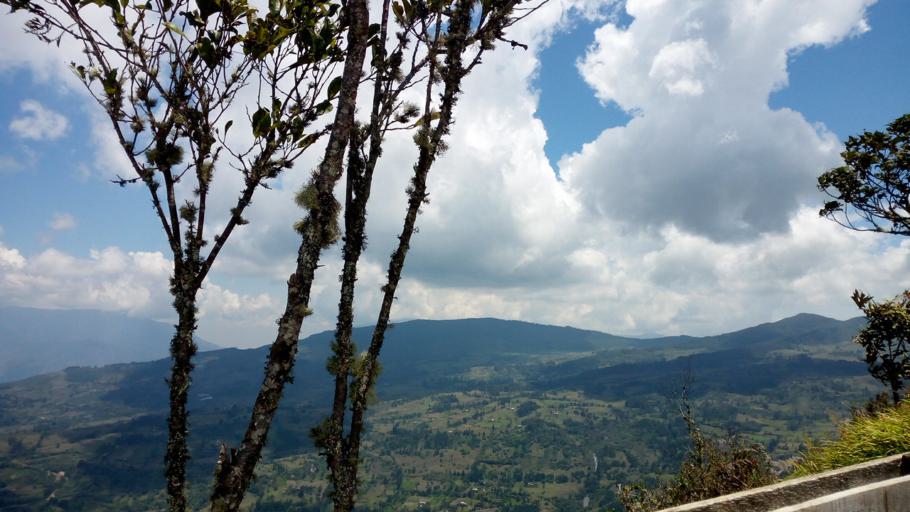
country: CO
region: Boyaca
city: Somondoco
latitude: 4.9708
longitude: -73.4129
